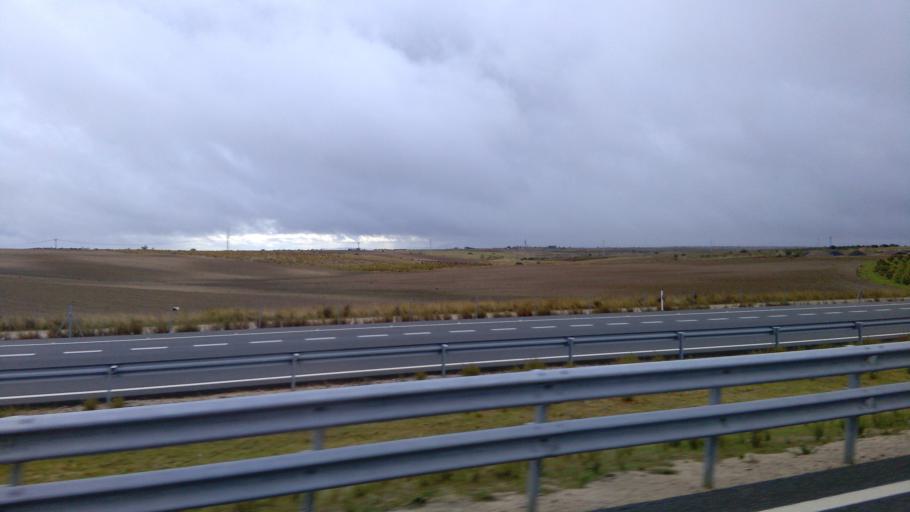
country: ES
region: Castille-La Mancha
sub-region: Province of Toledo
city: Las Ventas de Retamosa
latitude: 40.1857
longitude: -4.1309
